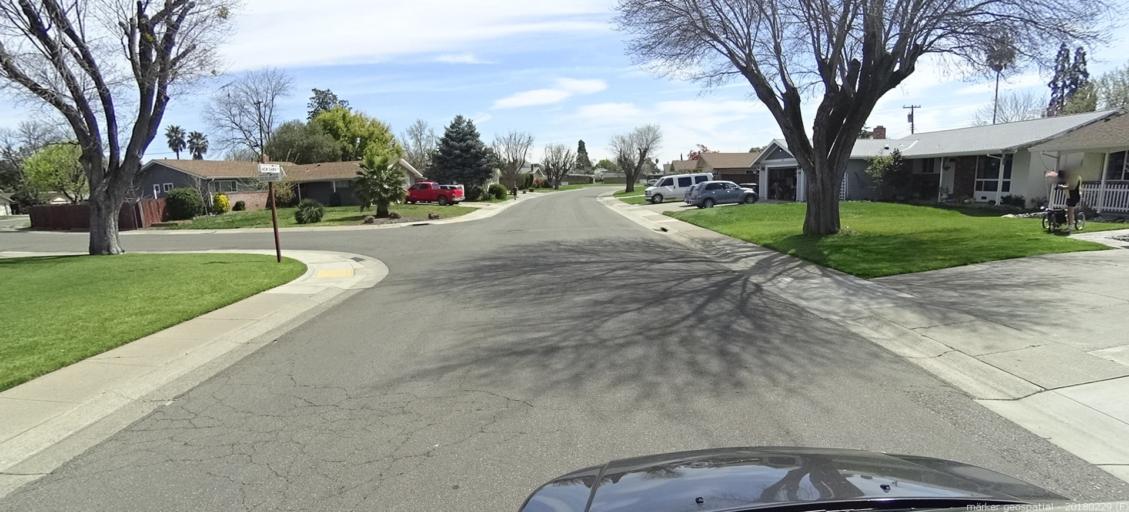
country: US
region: California
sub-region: Sacramento County
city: Rosemont
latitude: 38.5535
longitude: -121.3652
